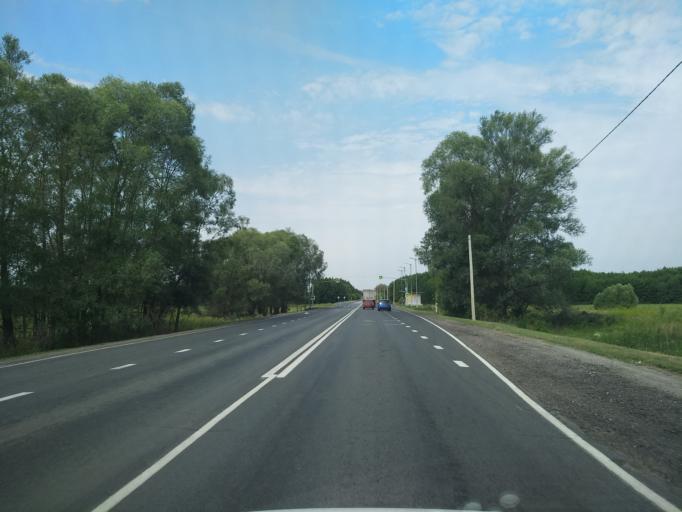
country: RU
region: Voronezj
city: Orlovo
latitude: 51.6807
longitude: 39.6016
